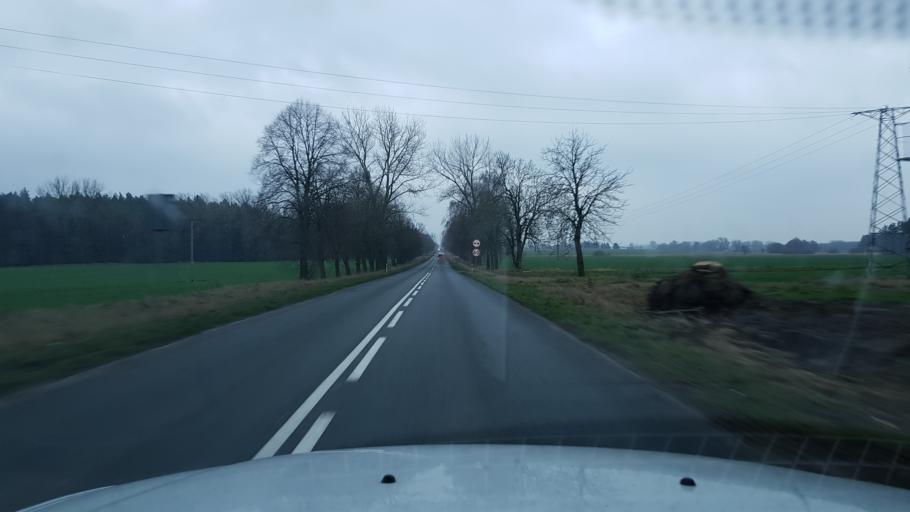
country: PL
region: West Pomeranian Voivodeship
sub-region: Powiat gryficki
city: Gryfice
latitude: 53.8970
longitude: 15.2050
